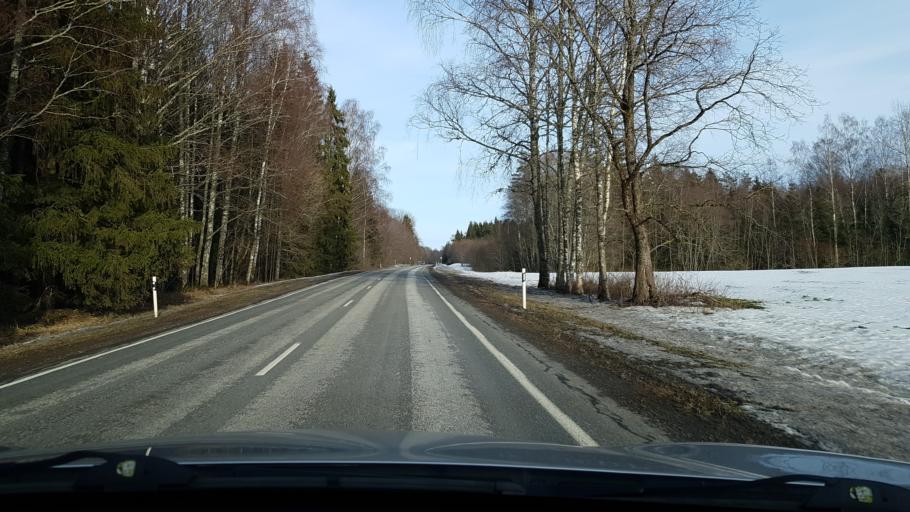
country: EE
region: Viljandimaa
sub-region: Abja vald
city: Abja-Paluoja
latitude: 58.3440
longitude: 25.3560
